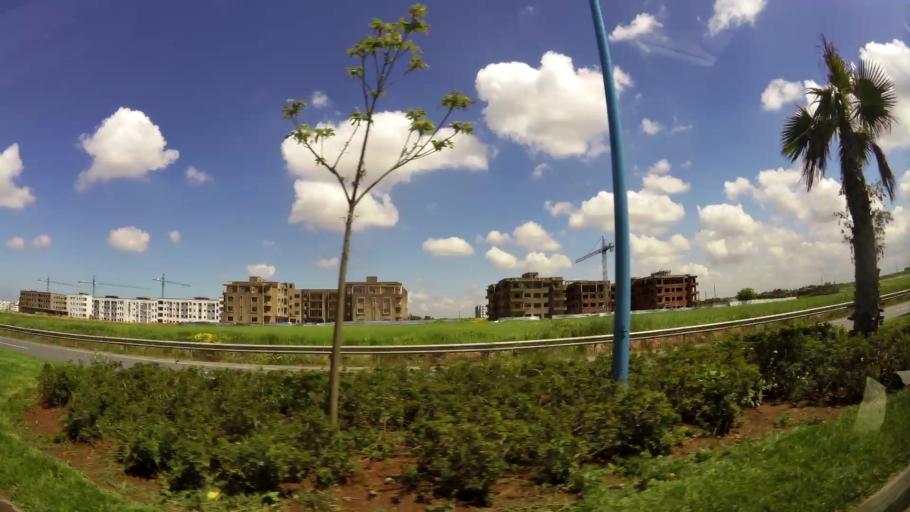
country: MA
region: Grand Casablanca
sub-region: Casablanca
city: Casablanca
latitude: 33.5194
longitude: -7.6156
